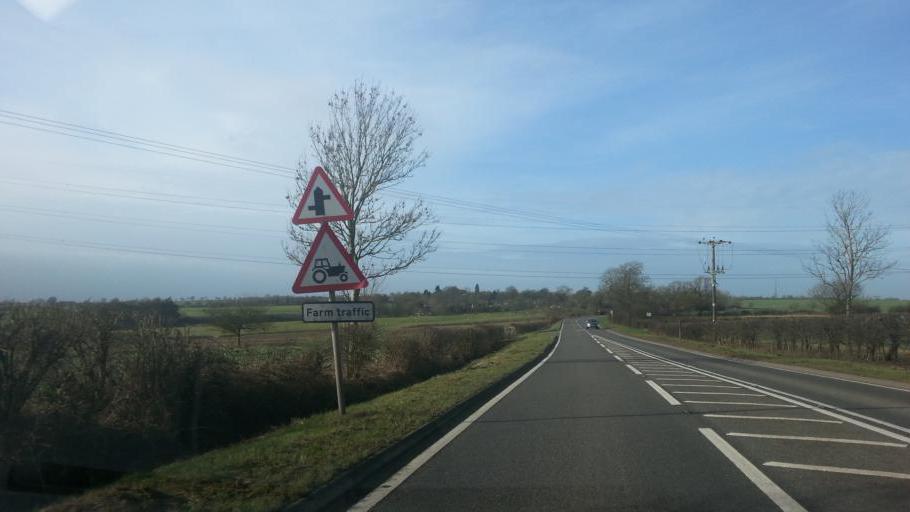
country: GB
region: England
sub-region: Leicestershire
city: Houghton on the Hill
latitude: 52.6124
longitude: -0.8909
